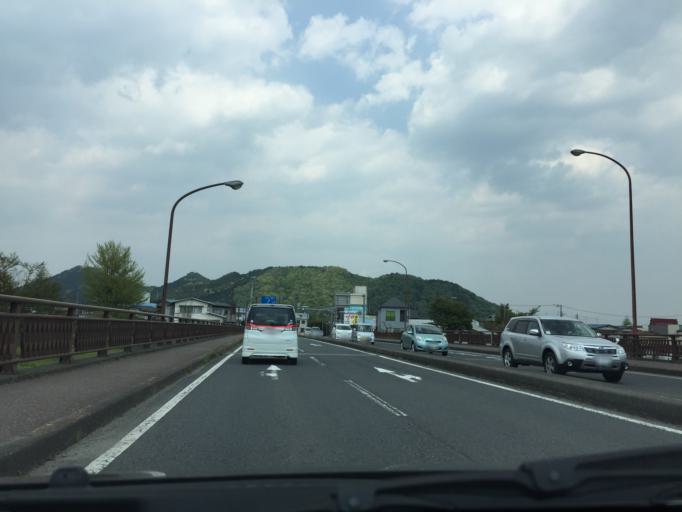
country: JP
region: Tochigi
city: Imaichi
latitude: 36.7317
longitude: 139.6878
